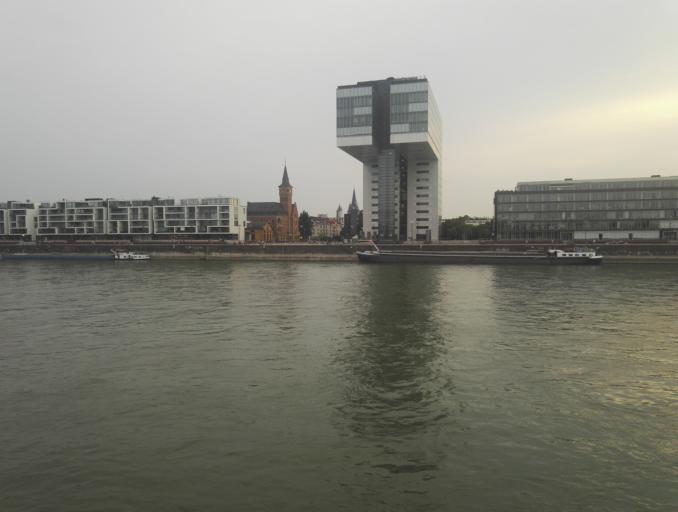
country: DE
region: North Rhine-Westphalia
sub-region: Regierungsbezirk Koln
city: Deutz
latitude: 50.9270
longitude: 6.9695
